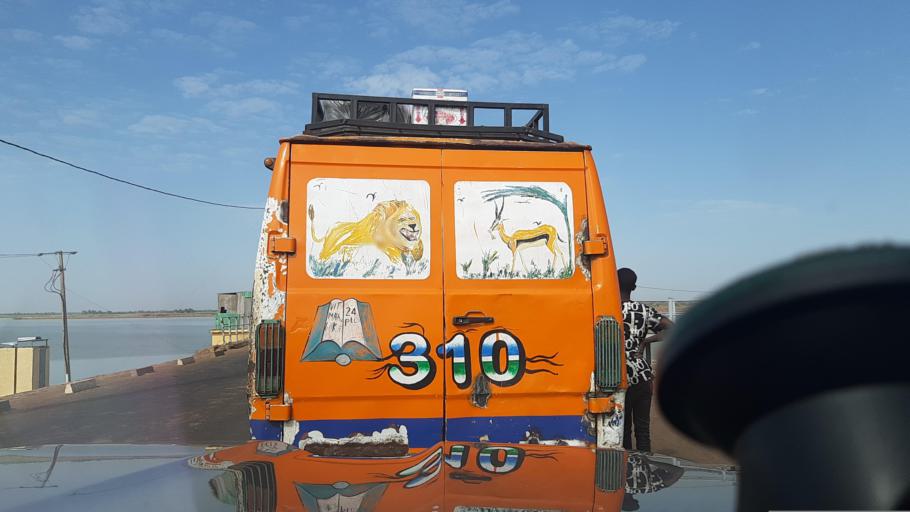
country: ML
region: Segou
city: Markala
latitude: 13.6787
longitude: -6.0769
